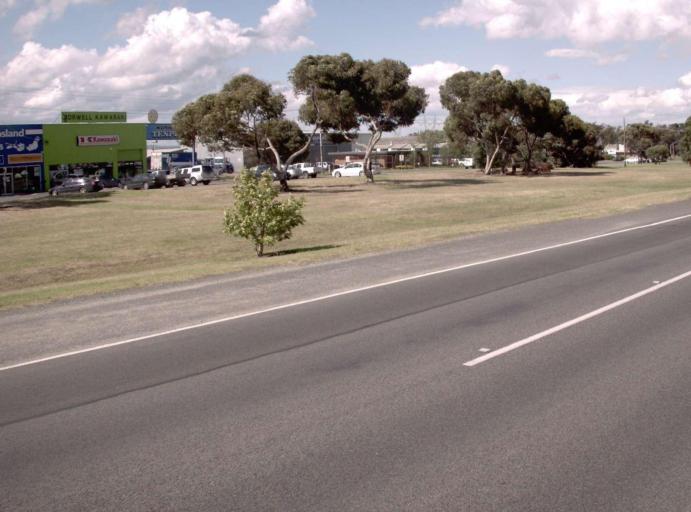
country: AU
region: Victoria
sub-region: Latrobe
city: Morwell
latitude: -38.2334
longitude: 146.4377
